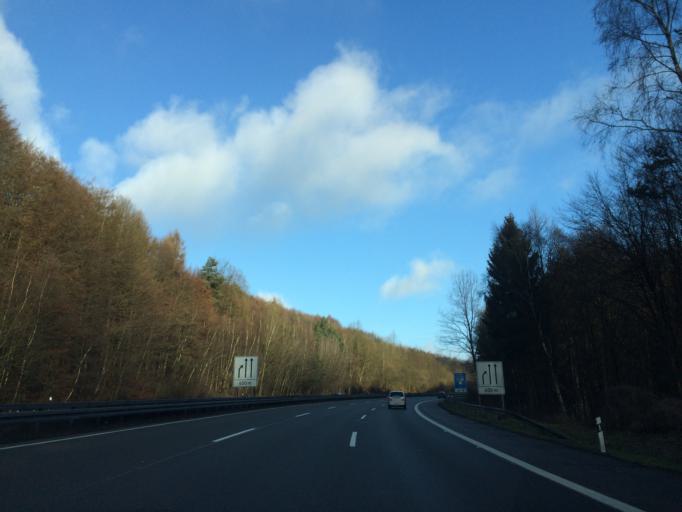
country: DE
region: Hesse
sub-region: Regierungsbezirk Kassel
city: Kirchheim
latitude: 50.8037
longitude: 9.5348
